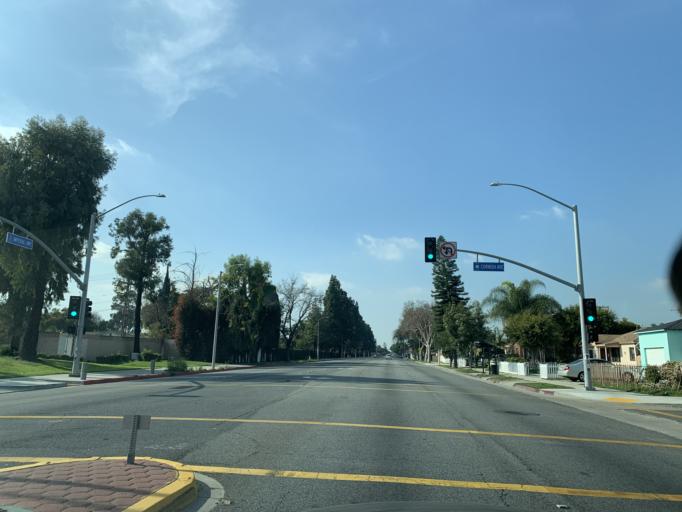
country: US
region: California
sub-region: Los Angeles County
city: Lynwood
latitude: 33.9315
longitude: -118.1919
